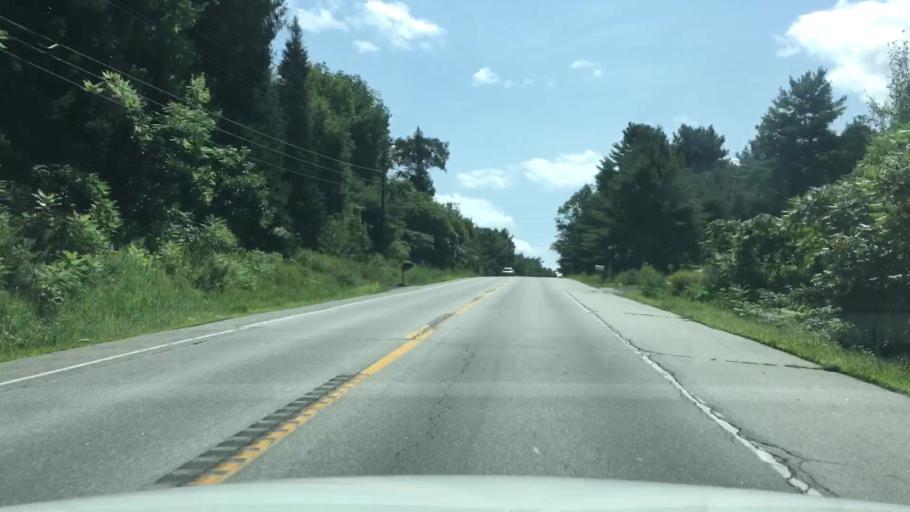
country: US
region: Maine
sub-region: Kennebec County
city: Farmingdale
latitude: 44.2681
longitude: -69.7657
